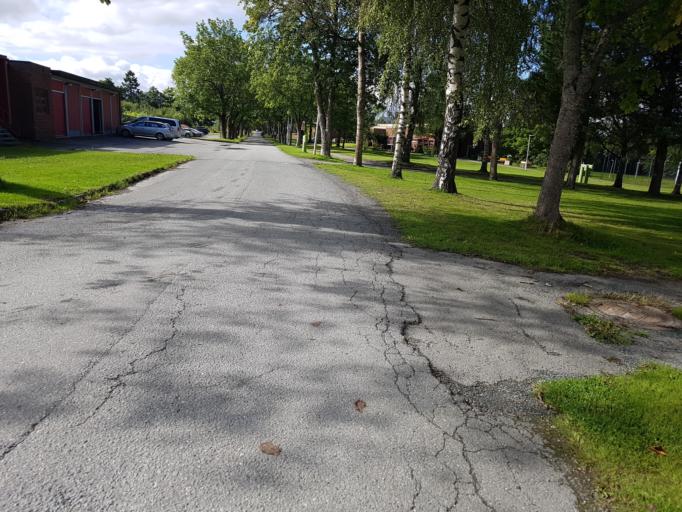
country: NO
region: Sor-Trondelag
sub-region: Trondheim
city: Trondheim
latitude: 63.4194
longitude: 10.4563
